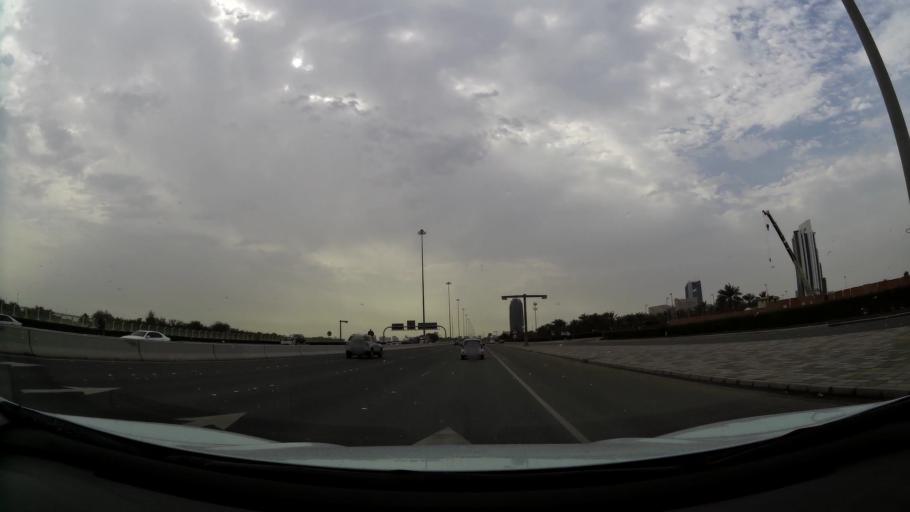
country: AE
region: Abu Dhabi
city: Abu Dhabi
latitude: 24.4691
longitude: 54.3941
